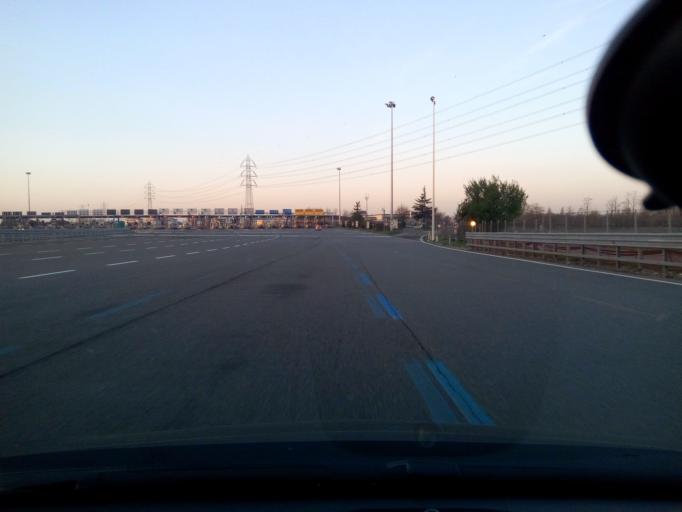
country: IT
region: Lombardy
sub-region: Citta metropolitana di Milano
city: Passirana
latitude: 45.5436
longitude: 9.0590
